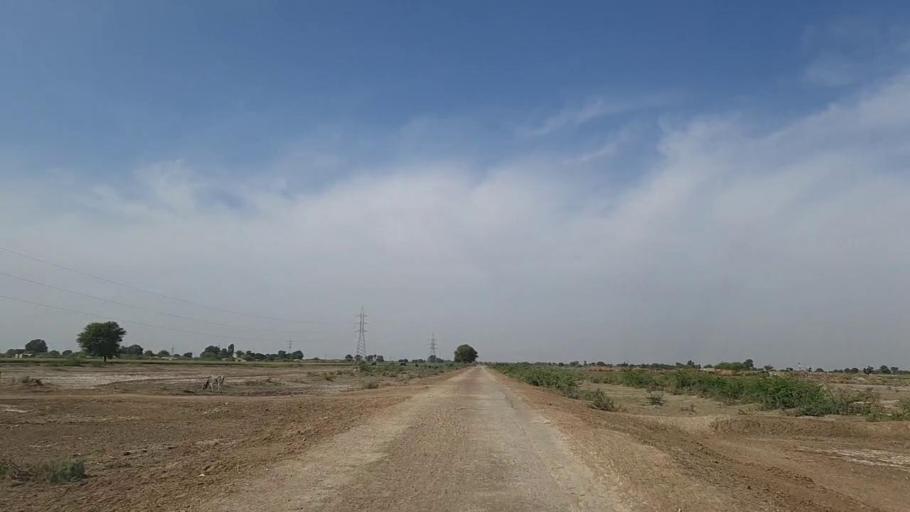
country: PK
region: Sindh
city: Samaro
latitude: 25.2185
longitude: 69.4516
